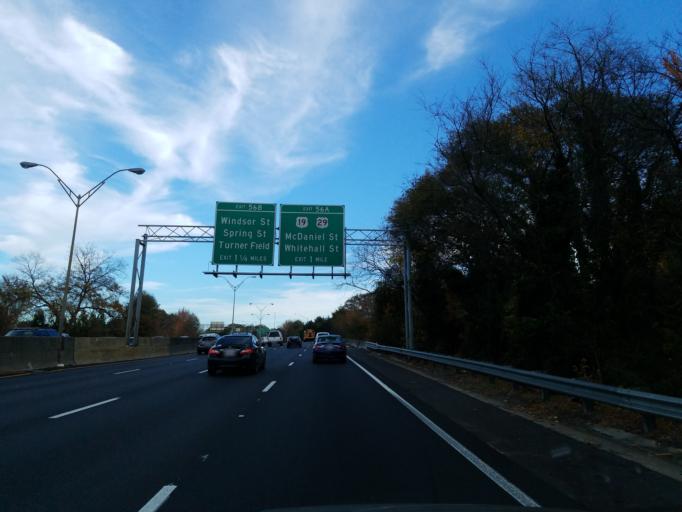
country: US
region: Georgia
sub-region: Fulton County
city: Atlanta
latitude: 33.7427
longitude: -84.4228
